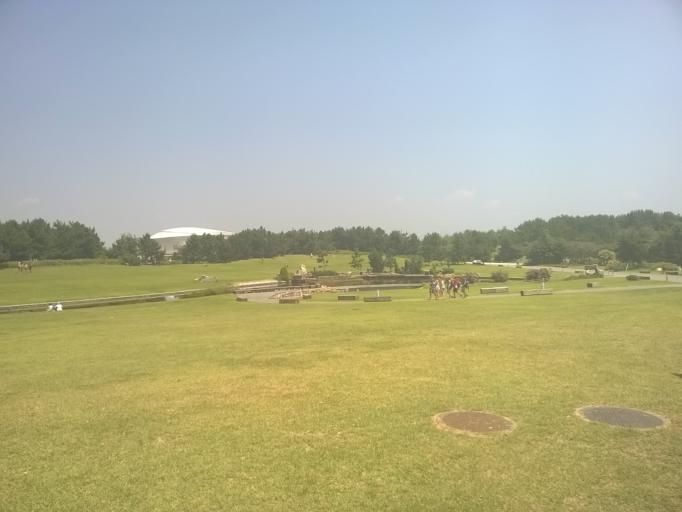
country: JP
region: Yamaguchi
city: Ogori-shimogo
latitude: 34.0060
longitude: 131.3716
